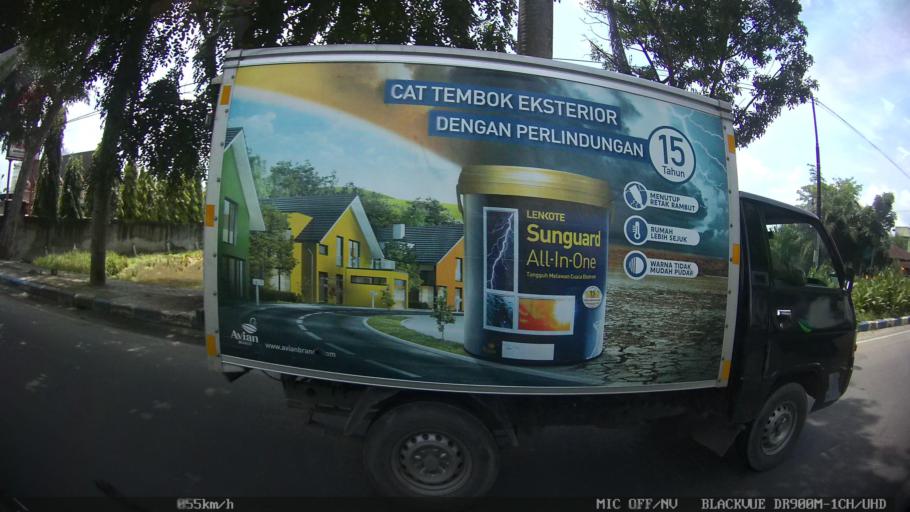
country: ID
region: North Sumatra
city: Percut
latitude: 3.5519
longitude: 98.8580
